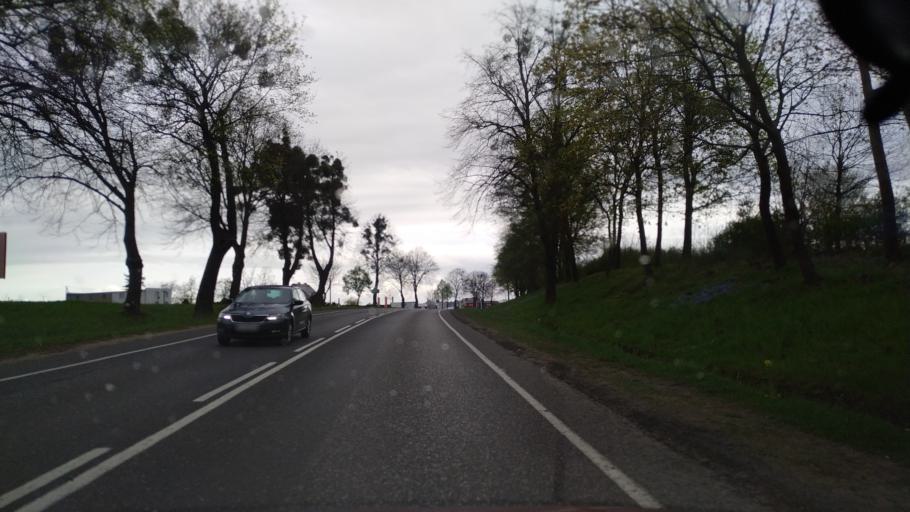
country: PL
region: Pomeranian Voivodeship
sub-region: Powiat starogardzki
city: Starogard Gdanski
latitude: 53.9480
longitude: 18.4698
